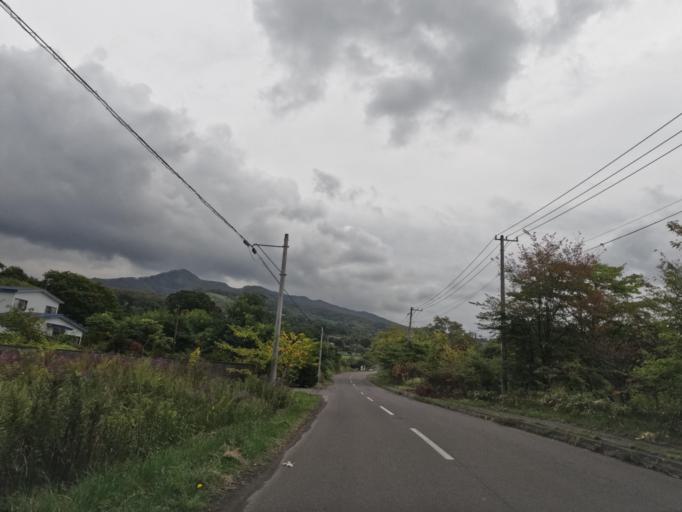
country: JP
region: Hokkaido
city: Date
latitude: 42.4552
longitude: 140.9039
